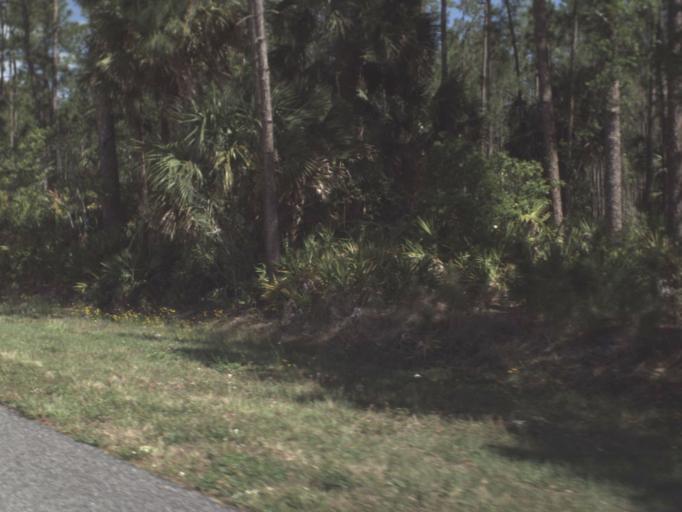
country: US
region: Florida
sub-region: Volusia County
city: Ormond-by-the-Sea
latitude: 29.3528
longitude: -81.1539
